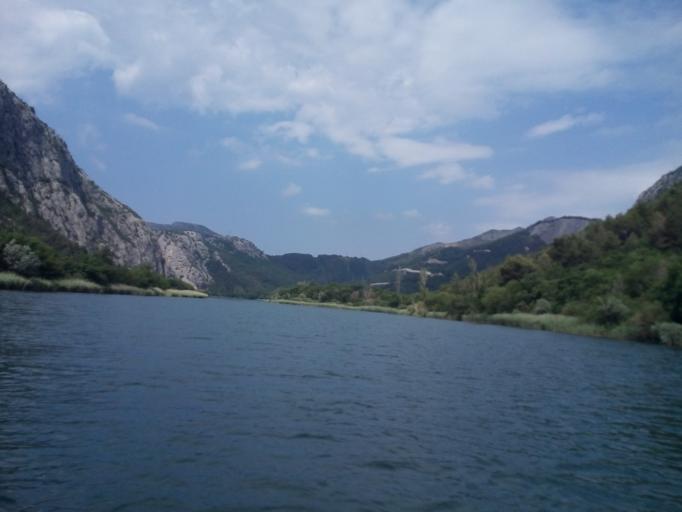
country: HR
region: Splitsko-Dalmatinska
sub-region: Grad Omis
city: Omis
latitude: 43.4494
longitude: 16.7165
